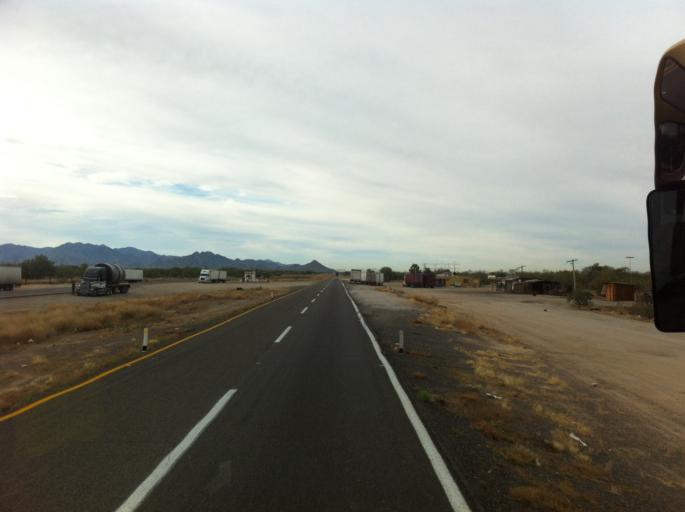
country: MX
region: Sonora
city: Hermosillo
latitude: 28.7353
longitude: -110.9774
